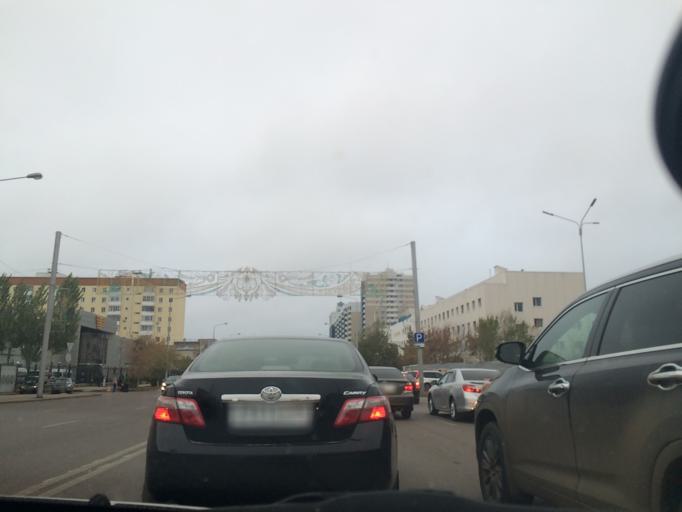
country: KZ
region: Astana Qalasy
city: Astana
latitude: 51.1713
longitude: 71.4074
